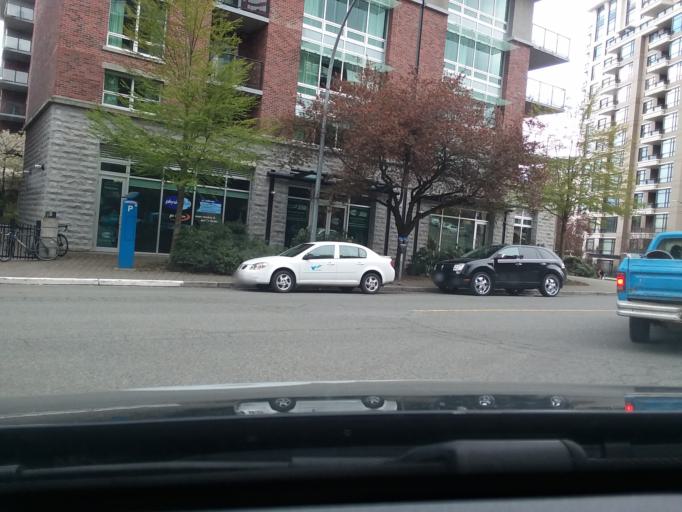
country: CA
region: British Columbia
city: Victoria
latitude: 48.4210
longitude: -123.3625
